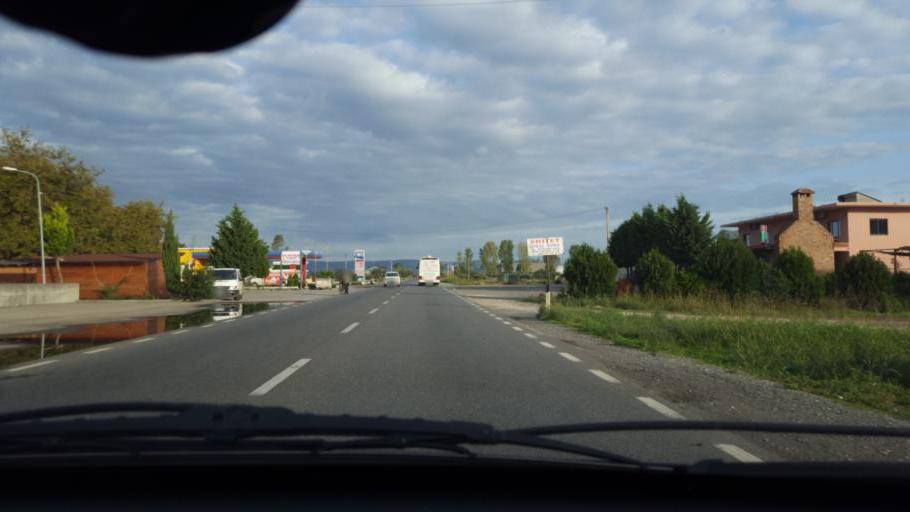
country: AL
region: Lezhe
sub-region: Rrethi i Lezhes
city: Zejmen
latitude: 41.7222
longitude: 19.6620
